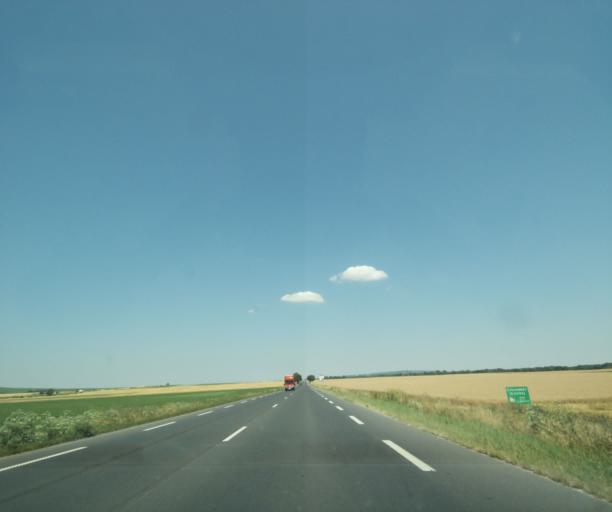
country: FR
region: Champagne-Ardenne
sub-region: Departement de la Marne
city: Verzy
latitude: 49.1506
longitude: 4.2126
